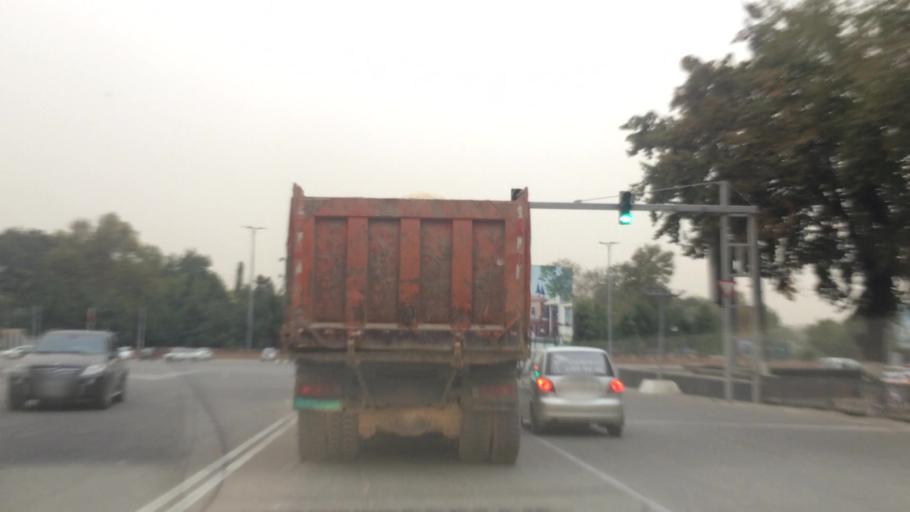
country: UZ
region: Toshkent Shahri
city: Tashkent
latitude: 41.3048
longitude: 69.2479
